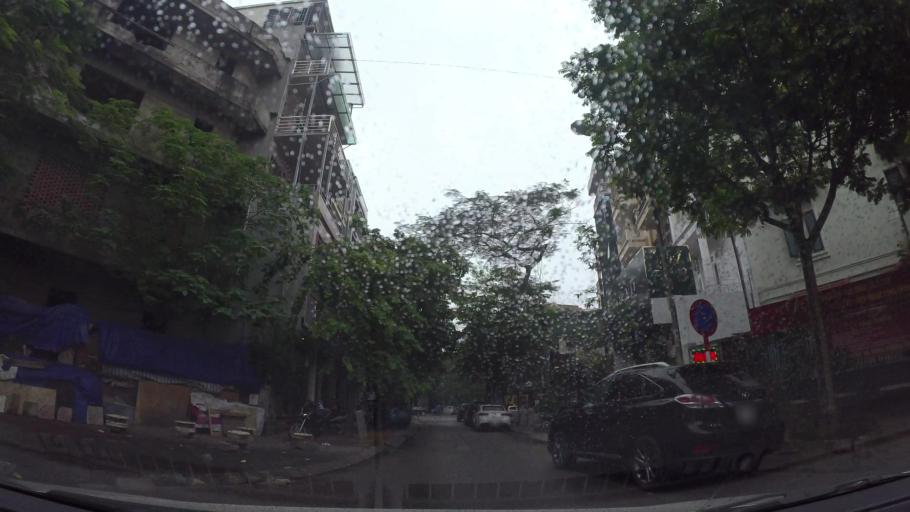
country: VN
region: Ha Noi
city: Cau Giay
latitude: 21.0162
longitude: 105.7992
